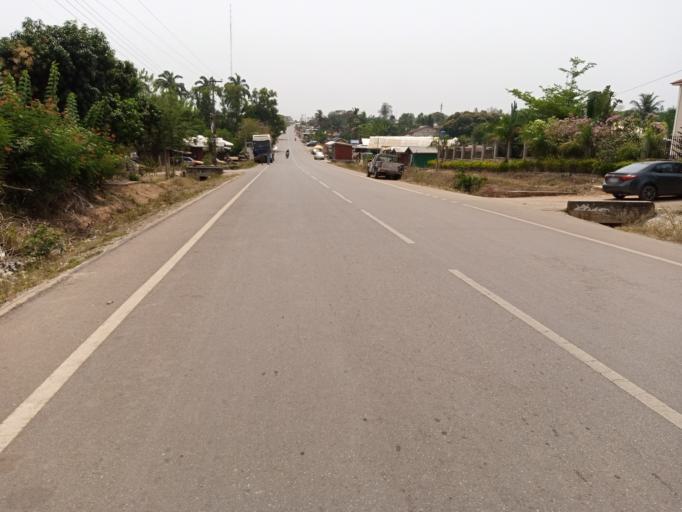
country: GH
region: Volta
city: Kpandu
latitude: 7.0082
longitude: 0.2958
